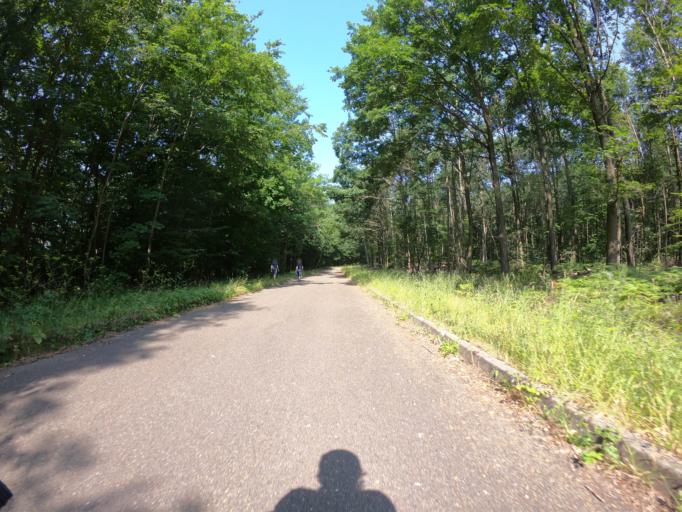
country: FR
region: Ile-de-France
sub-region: Departement de l'Essonne
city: Igny
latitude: 48.7534
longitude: 2.2354
